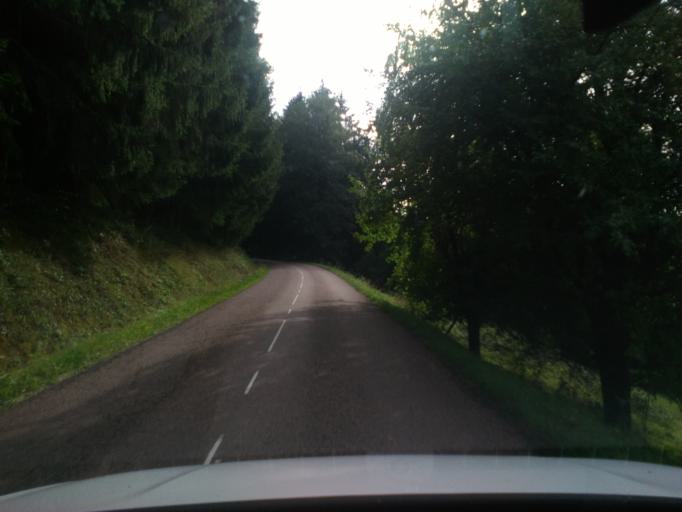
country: FR
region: Lorraine
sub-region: Departement des Vosges
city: Saint-Die-des-Vosges
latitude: 48.3312
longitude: 6.9846
